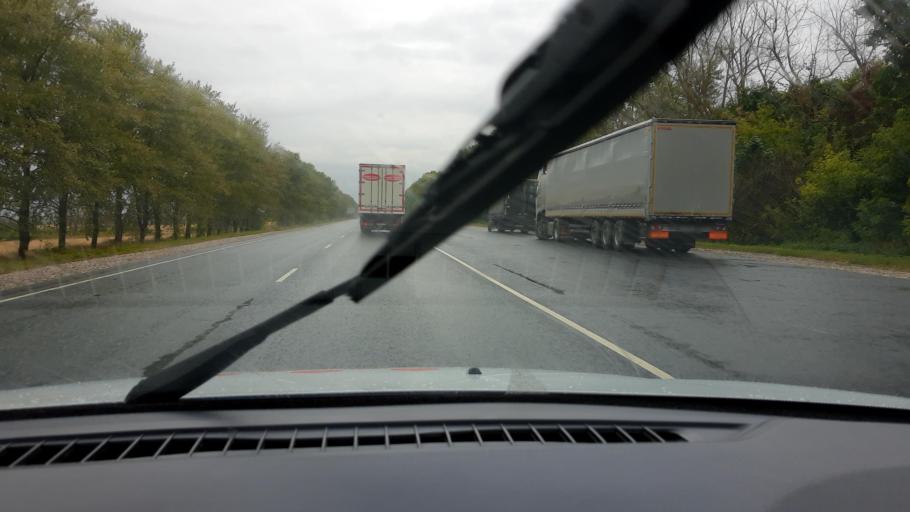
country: RU
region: Chuvashia
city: Yantikovo
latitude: 55.7894
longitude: 47.7094
